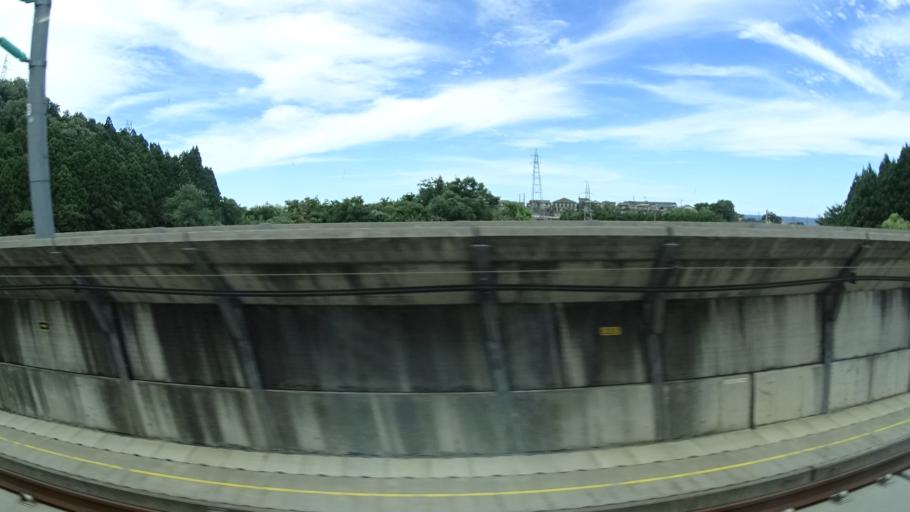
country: JP
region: Niigata
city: Itoigawa
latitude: 37.0194
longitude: 137.8000
